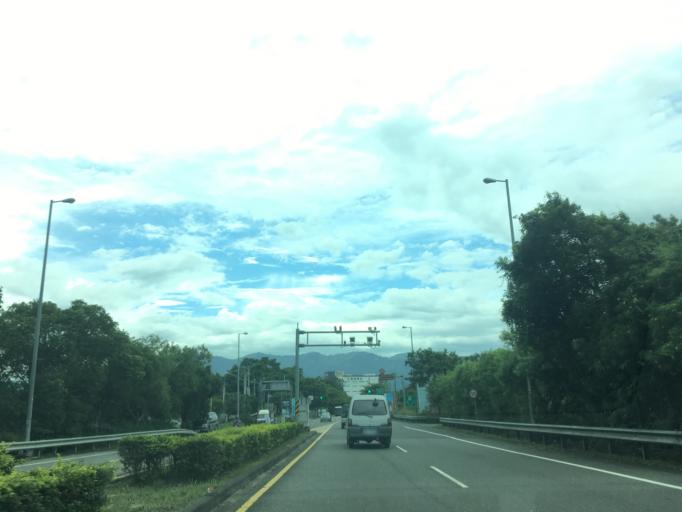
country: TW
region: Taiwan
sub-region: Yunlin
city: Douliu
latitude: 23.5950
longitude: 120.5241
